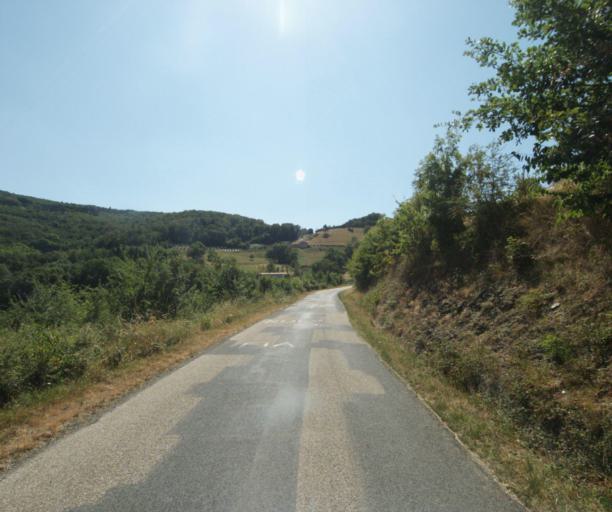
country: FR
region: Rhone-Alpes
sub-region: Departement du Rhone
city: Courzieu
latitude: 45.7308
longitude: 4.5588
